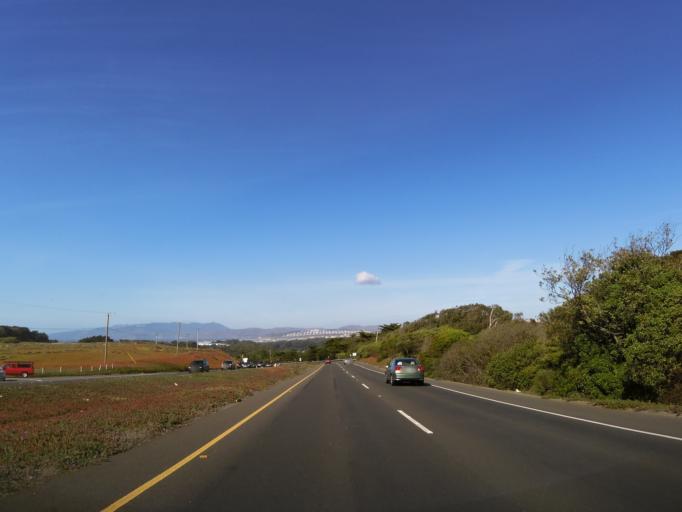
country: US
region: California
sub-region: San Mateo County
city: Broadmoor
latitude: 37.7132
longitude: -122.4981
